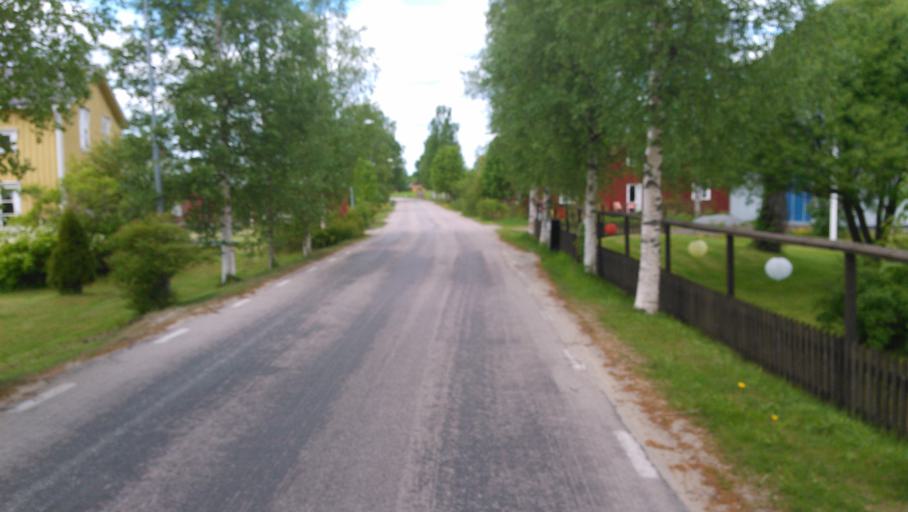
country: SE
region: Vaesterbotten
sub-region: Umea Kommun
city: Roback
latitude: 63.8658
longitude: 20.0774
